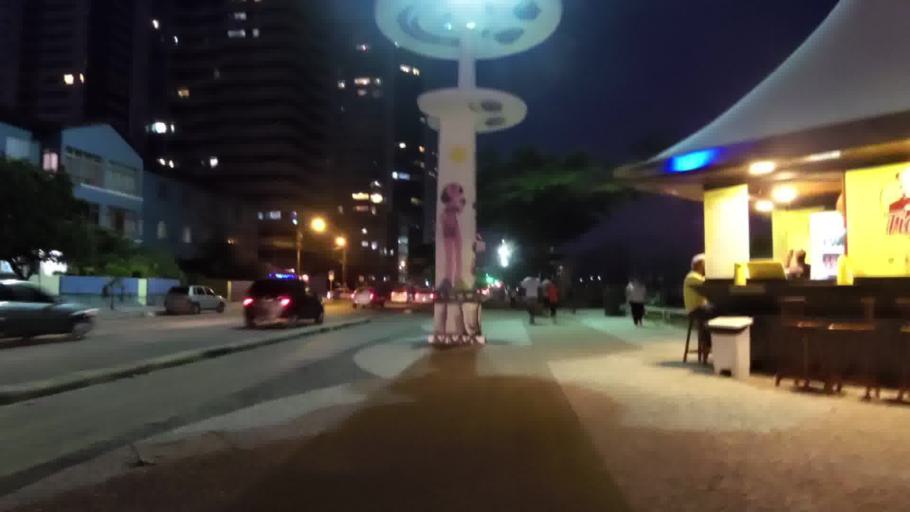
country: BR
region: Pernambuco
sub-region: Recife
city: Recife
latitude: -8.0968
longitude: -34.8832
